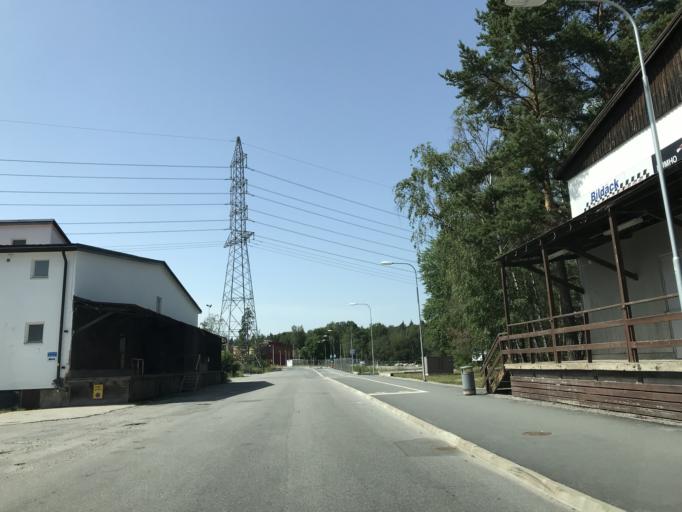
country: SE
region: Stockholm
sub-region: Solna Kommun
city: Rasunda
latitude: 59.3825
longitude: 17.9919
